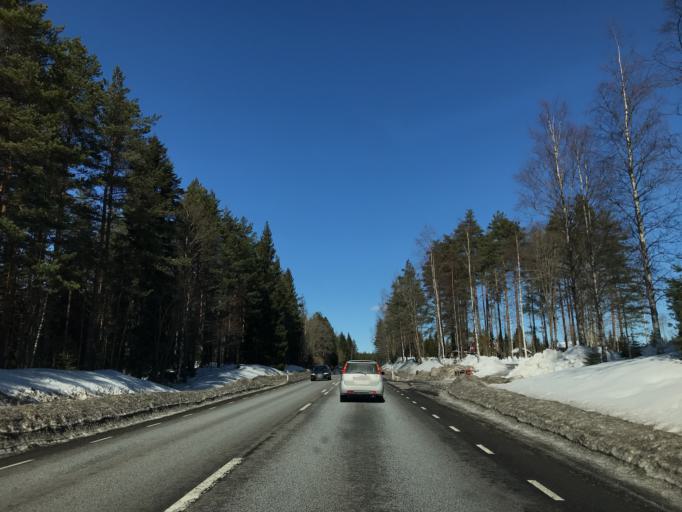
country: SE
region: Vaermland
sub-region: Filipstads Kommun
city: Filipstad
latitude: 59.7659
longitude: 14.2589
